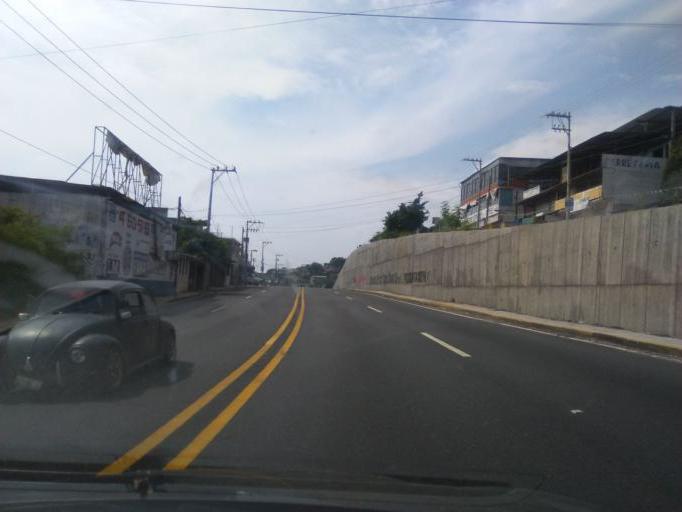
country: MX
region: Guerrero
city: Acapulco de Juarez
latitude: 16.8834
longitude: -99.9496
